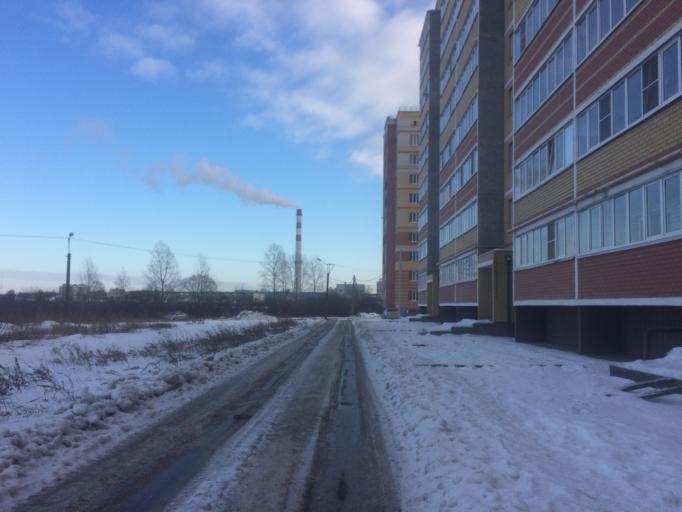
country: RU
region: Mariy-El
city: Yoshkar-Ola
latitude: 56.6406
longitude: 47.9279
